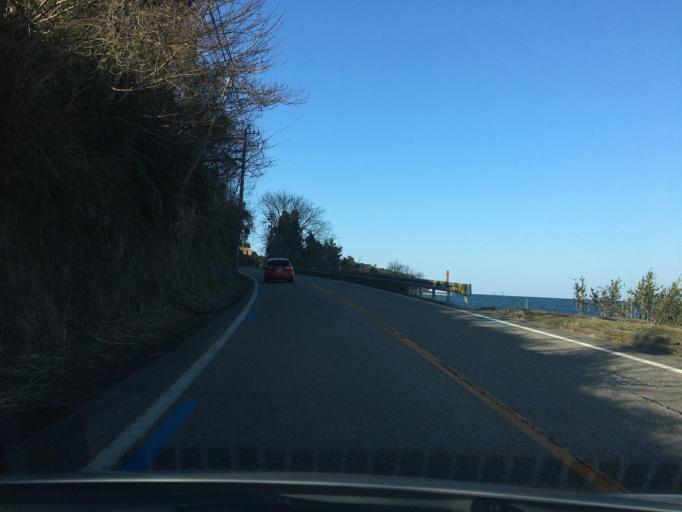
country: JP
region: Toyama
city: Himi
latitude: 36.9042
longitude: 137.0140
